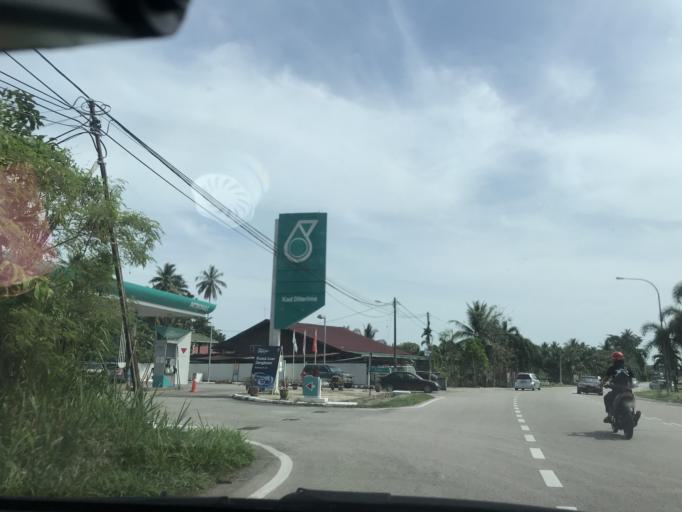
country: MY
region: Kelantan
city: Tumpat
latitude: 6.1857
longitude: 102.1675
